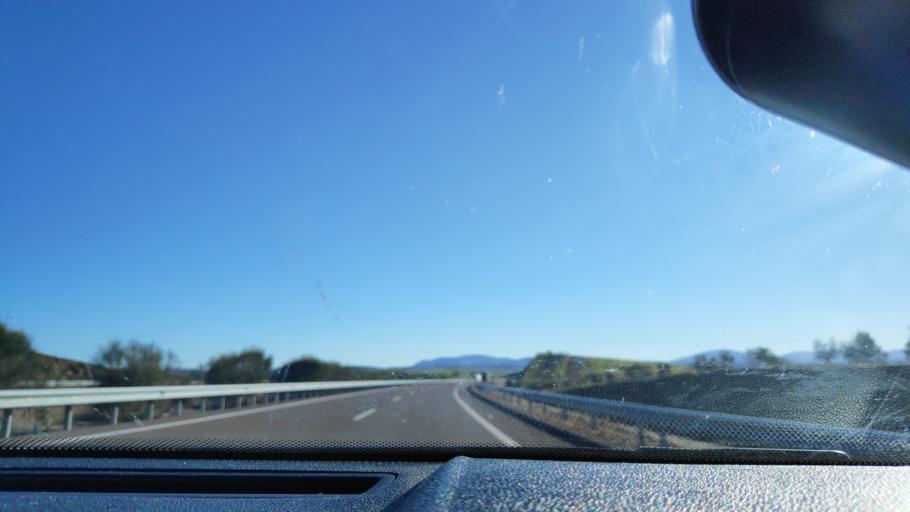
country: ES
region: Extremadura
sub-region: Provincia de Badajoz
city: Fuente de Cantos
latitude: 38.1880
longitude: -6.2794
